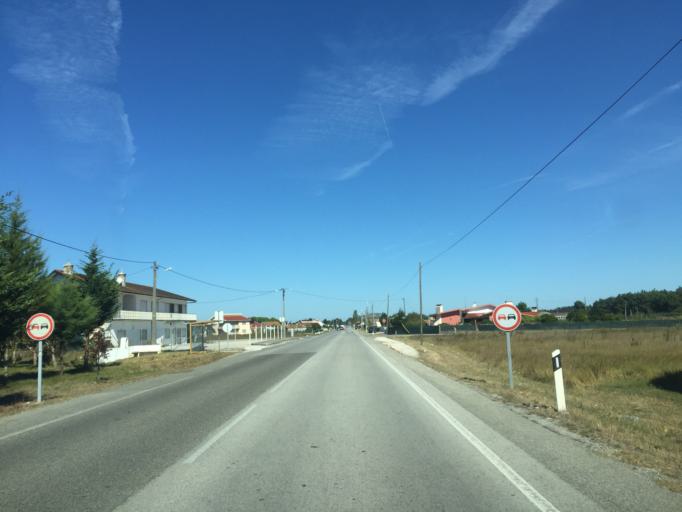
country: PT
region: Coimbra
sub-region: Figueira da Foz
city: Alhadas
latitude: 40.2292
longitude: -8.8012
